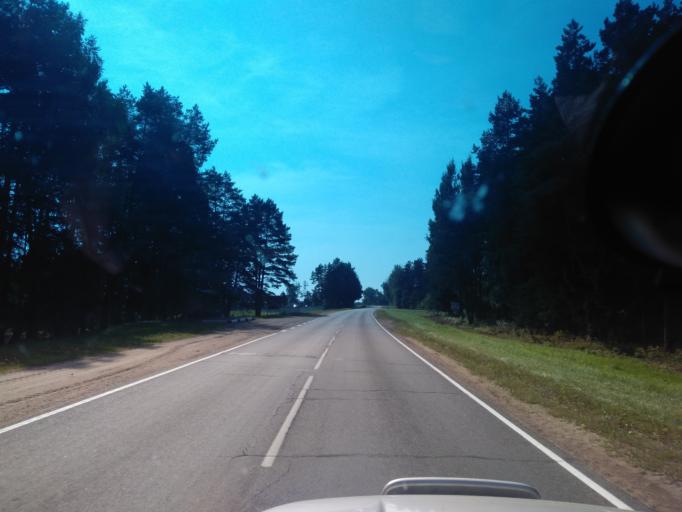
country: BY
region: Minsk
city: Uzda
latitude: 53.4225
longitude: 27.2139
